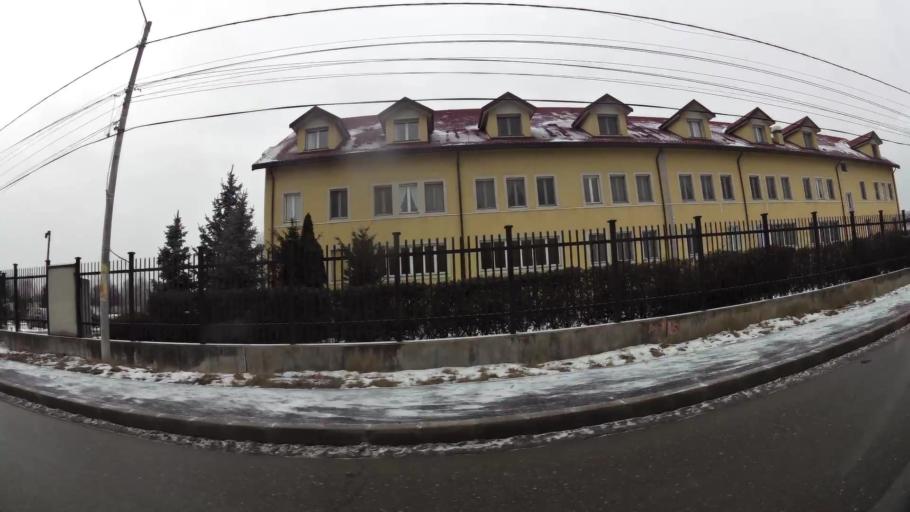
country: RO
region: Dambovita
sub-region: Municipiul Targoviste
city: Targoviste
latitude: 44.9360
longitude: 25.4713
